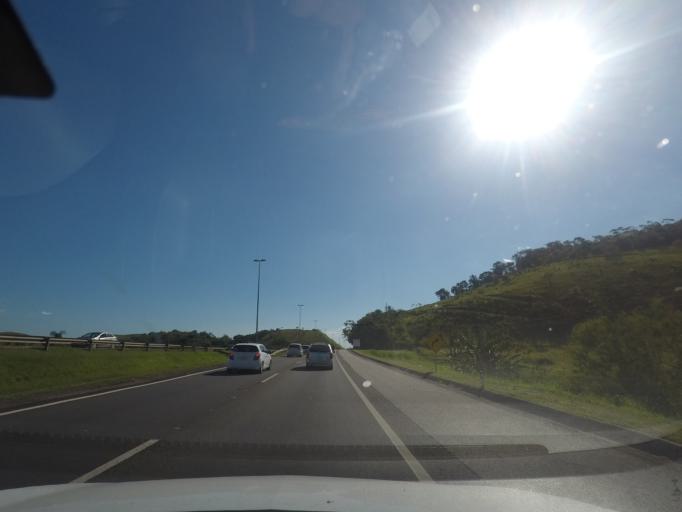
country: BR
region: Rio de Janeiro
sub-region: Guapimirim
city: Guapimirim
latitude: -22.6341
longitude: -43.0550
